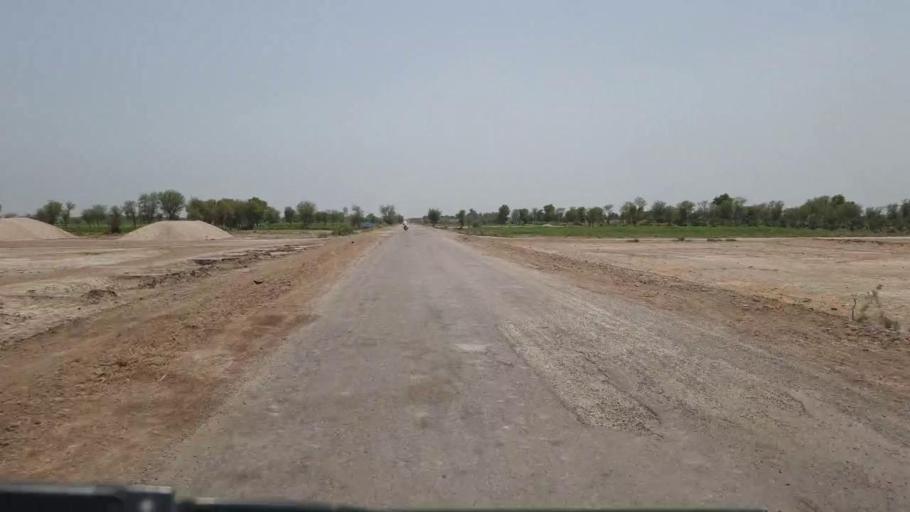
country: PK
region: Sindh
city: Daulatpur
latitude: 26.4493
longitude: 68.1169
